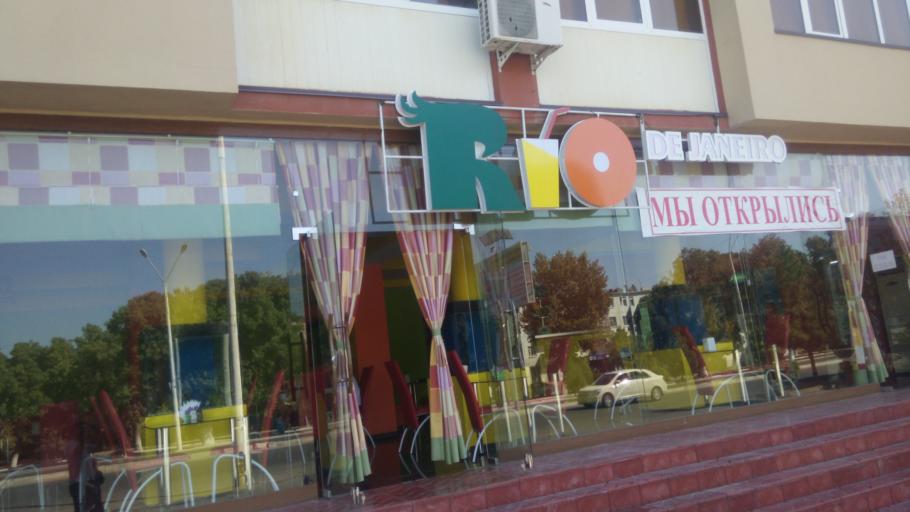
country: UZ
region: Bukhara
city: Bukhara
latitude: 39.7591
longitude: 64.4327
